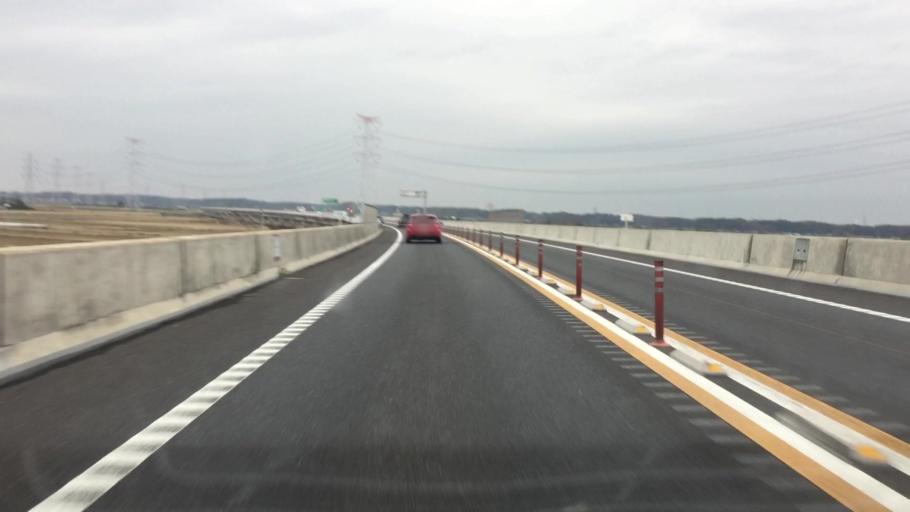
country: JP
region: Ibaraki
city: Inashiki
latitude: 35.9107
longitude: 140.3689
